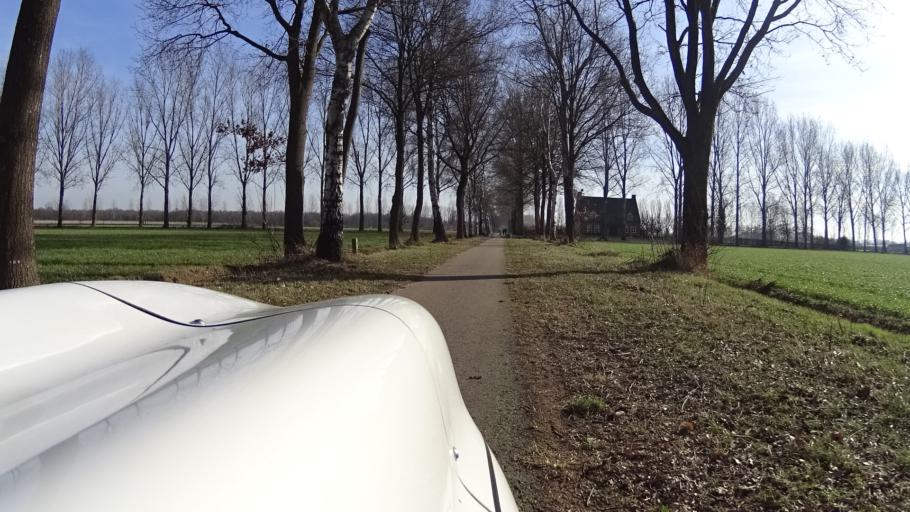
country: NL
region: North Brabant
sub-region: Gemeente Veghel
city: Mariaheide
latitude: 51.6188
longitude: 5.5686
